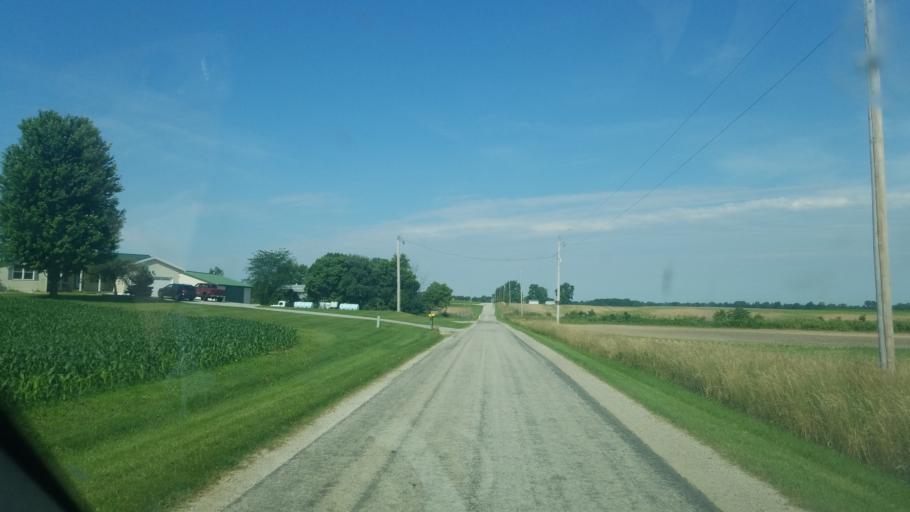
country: US
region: Ohio
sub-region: Wyandot County
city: Upper Sandusky
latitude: 40.9204
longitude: -83.2105
